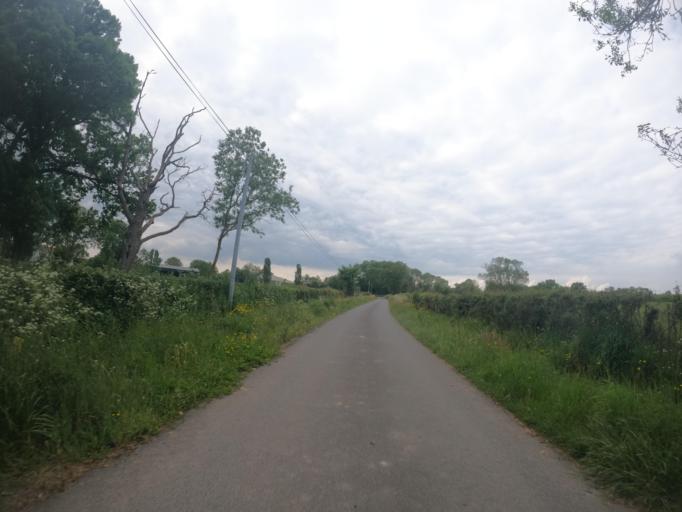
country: FR
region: Poitou-Charentes
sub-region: Departement des Deux-Sevres
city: Chiche
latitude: 46.8649
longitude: -0.3204
